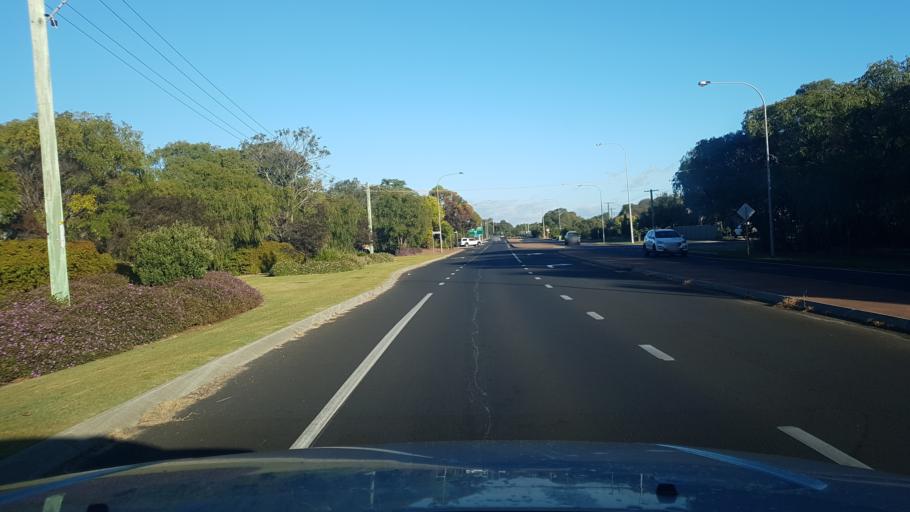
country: AU
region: Western Australia
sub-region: Busselton
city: Vasse
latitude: -33.6609
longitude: 115.2640
